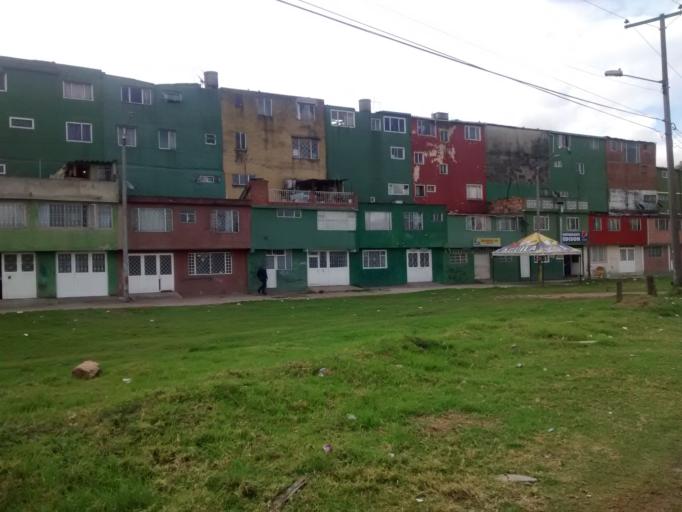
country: CO
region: Bogota D.C.
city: Barrio San Luis
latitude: 4.7122
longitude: -74.1077
